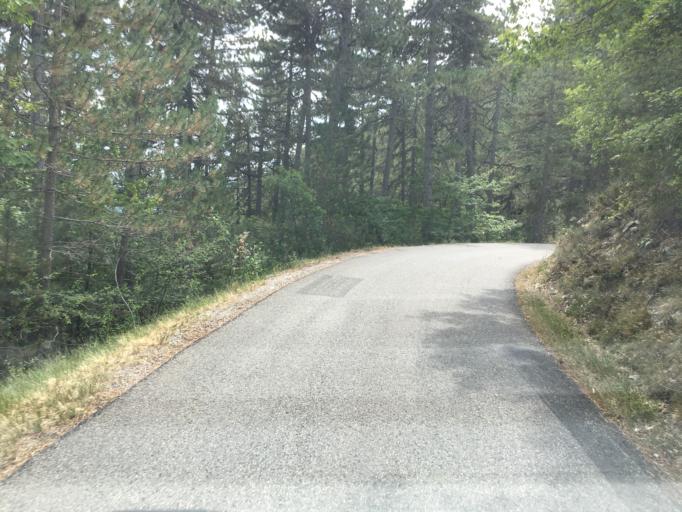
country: FR
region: Provence-Alpes-Cote d'Azur
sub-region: Departement des Alpes-de-Haute-Provence
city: Digne-les-Bains
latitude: 44.2111
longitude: 6.1501
